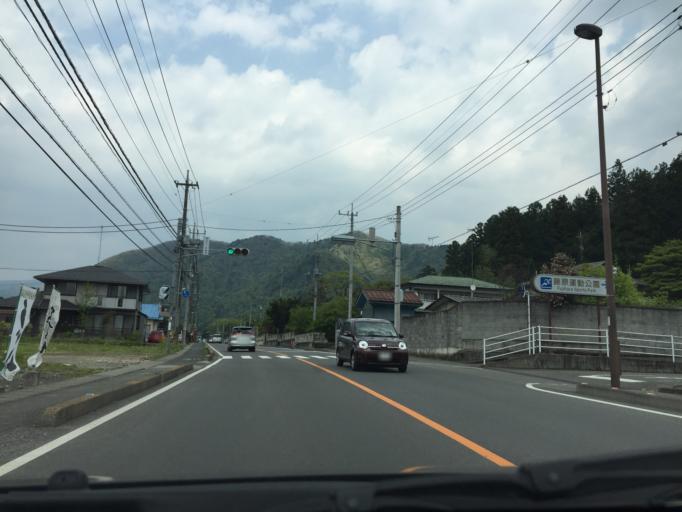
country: JP
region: Tochigi
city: Imaichi
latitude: 36.8147
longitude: 139.7137
